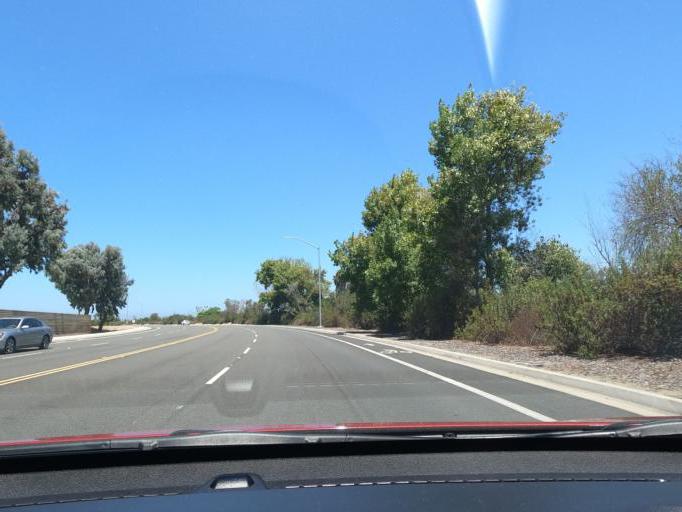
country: US
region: California
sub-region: San Diego County
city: Imperial Beach
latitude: 32.5514
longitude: -117.0560
